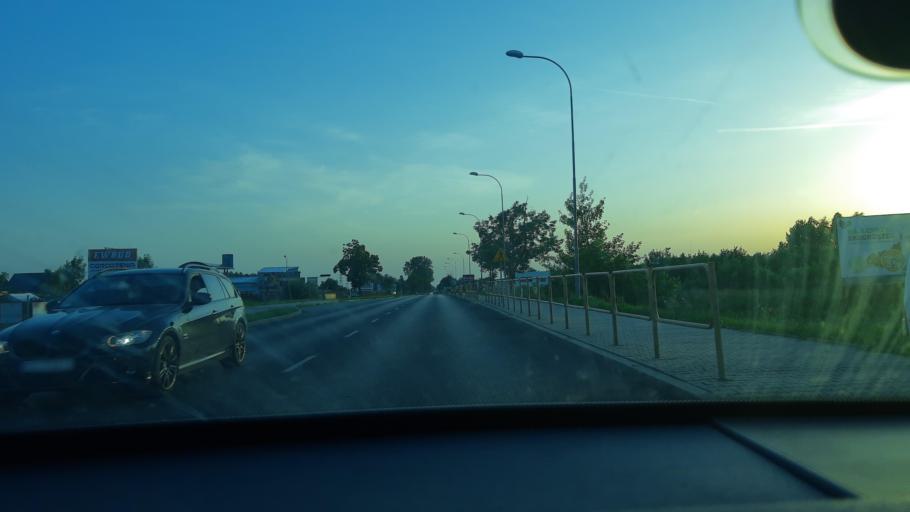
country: PL
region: Lodz Voivodeship
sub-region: Powiat zdunskowolski
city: Zdunska Wola
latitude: 51.6075
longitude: 18.8855
